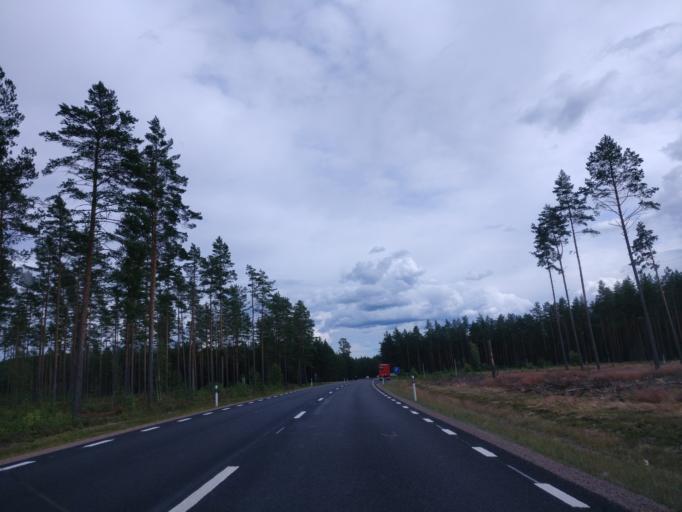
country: SE
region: Vaermland
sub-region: Hagfors Kommun
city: Hagfors
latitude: 60.0453
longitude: 13.5788
